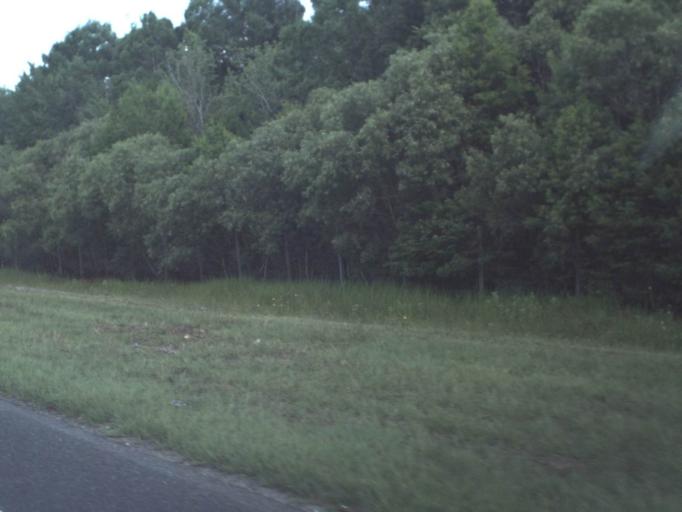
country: US
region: Florida
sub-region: Putnam County
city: Palatka
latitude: 29.6298
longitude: -81.7541
